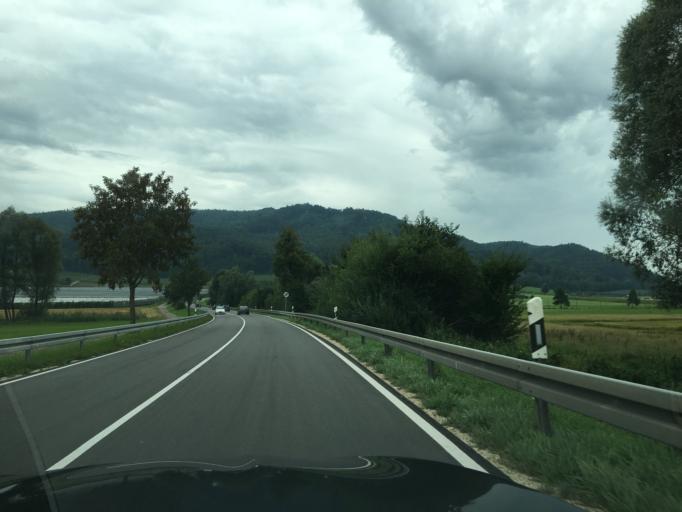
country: DE
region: Baden-Wuerttemberg
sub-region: Freiburg Region
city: Stockach
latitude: 47.8083
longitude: 8.9911
